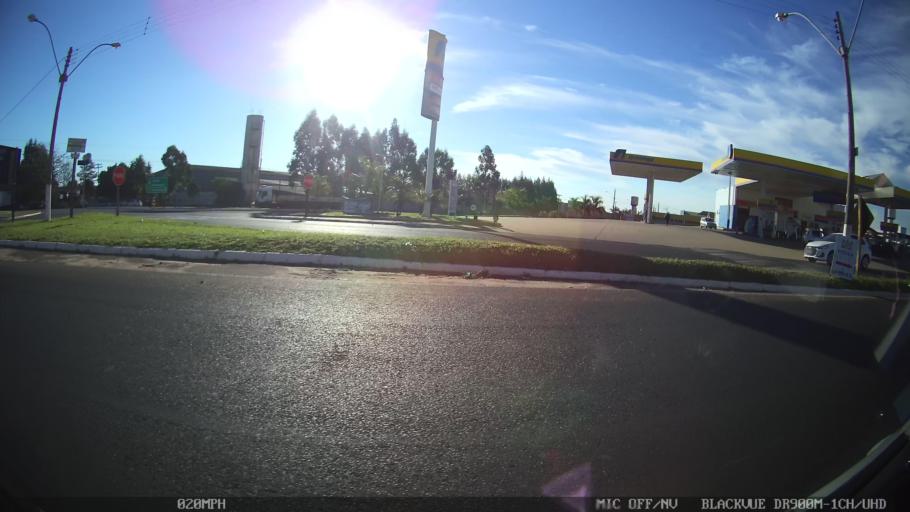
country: BR
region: Sao Paulo
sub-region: Americo Brasiliense
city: Americo Brasiliense
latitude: -21.7448
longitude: -48.1280
